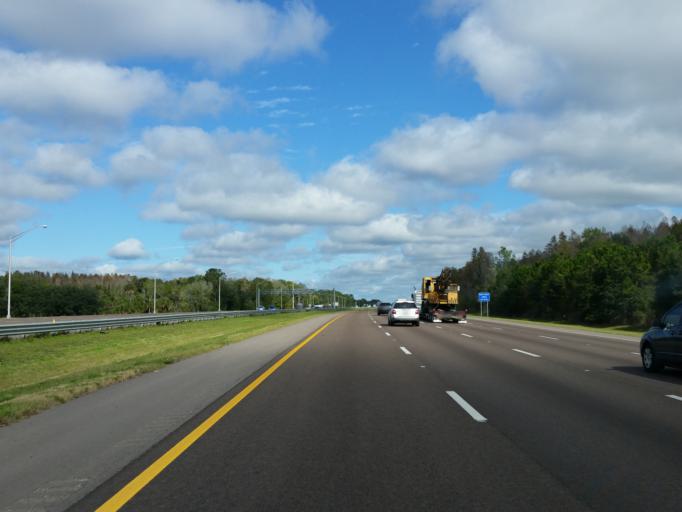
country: US
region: Florida
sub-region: Pasco County
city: Wesley Chapel
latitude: 28.2070
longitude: -82.3766
